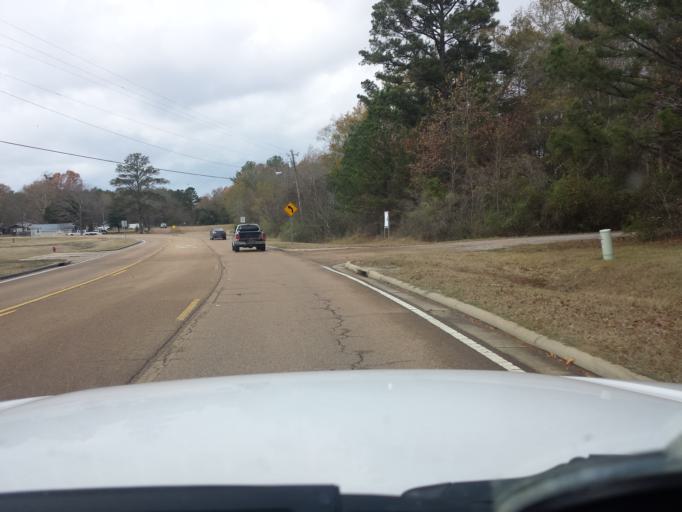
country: US
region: Mississippi
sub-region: Rankin County
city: Flowood
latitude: 32.3418
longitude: -90.0914
